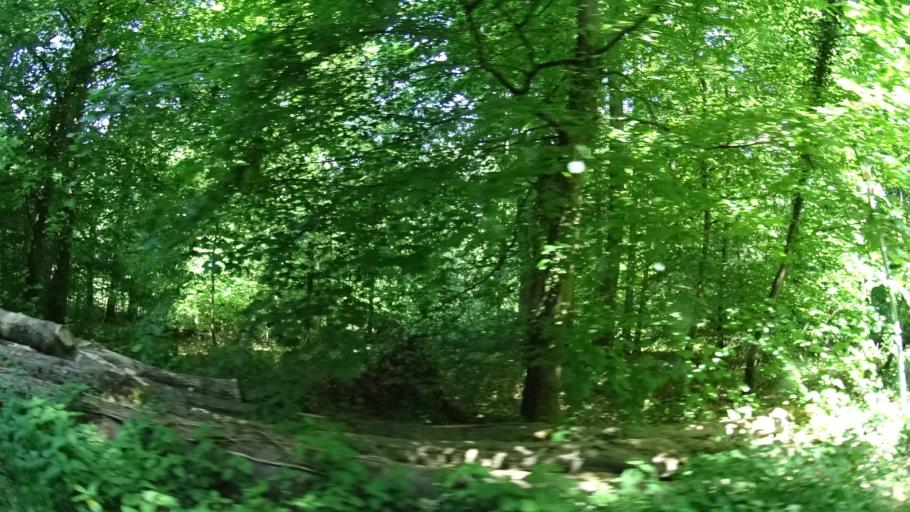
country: DE
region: Baden-Wuerttemberg
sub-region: Karlsruhe Region
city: Malsch
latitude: 48.8678
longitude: 8.3510
